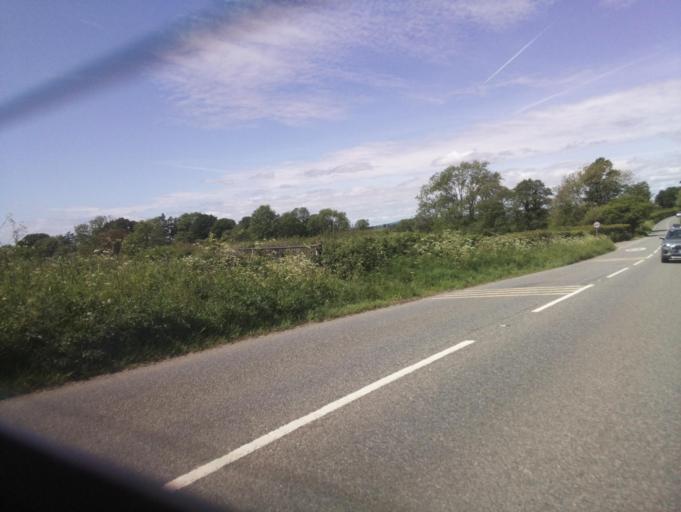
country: GB
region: England
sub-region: Devon
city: Ottery St Mary
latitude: 50.8236
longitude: -3.2848
